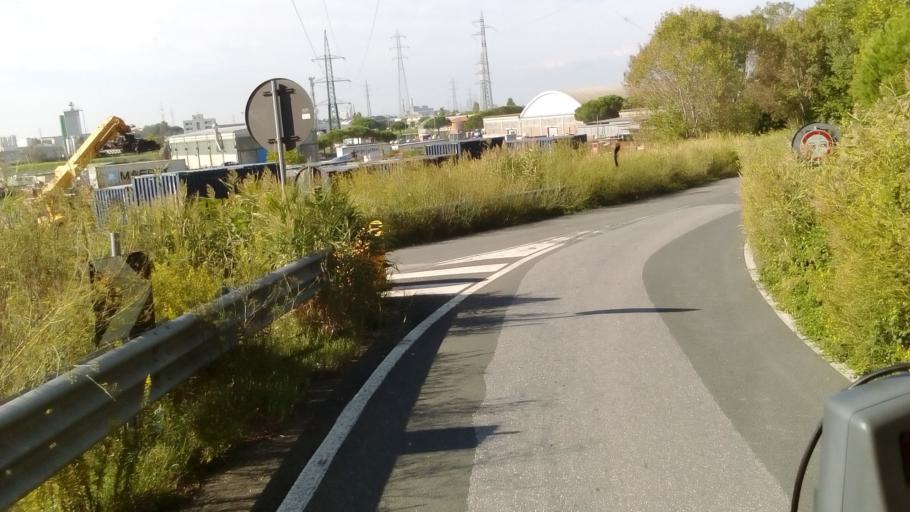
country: IT
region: Tuscany
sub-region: Provincia di Livorno
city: Livorno
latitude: 43.5799
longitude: 10.3488
